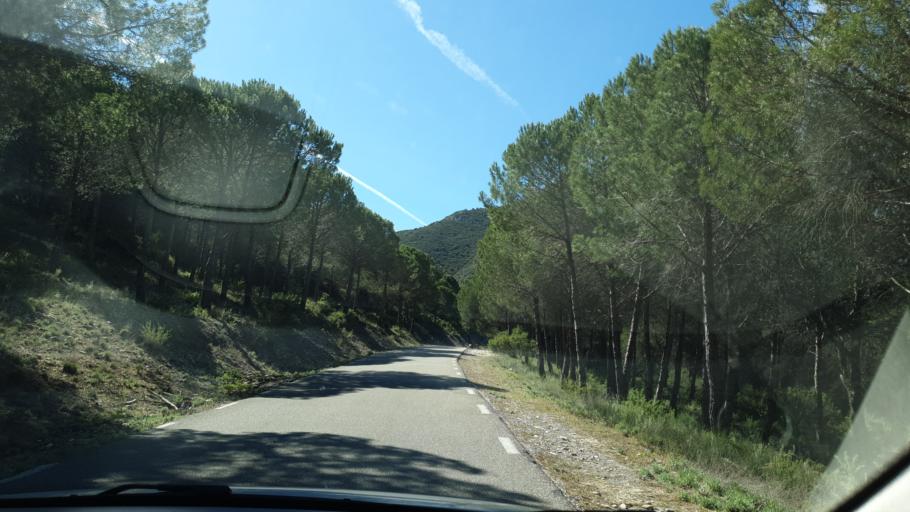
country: ES
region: Andalusia
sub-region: Provincia de Malaga
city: Ojen
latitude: 36.5924
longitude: -4.8574
